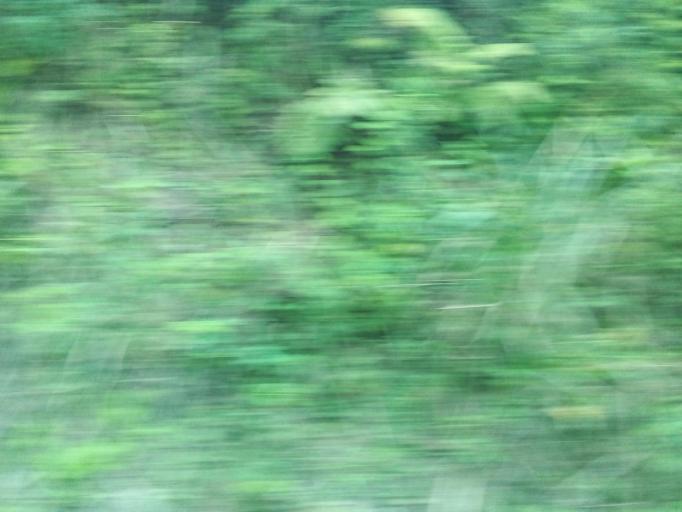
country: BR
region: Minas Gerais
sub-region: Joao Monlevade
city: Joao Monlevade
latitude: -19.8267
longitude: -43.1137
